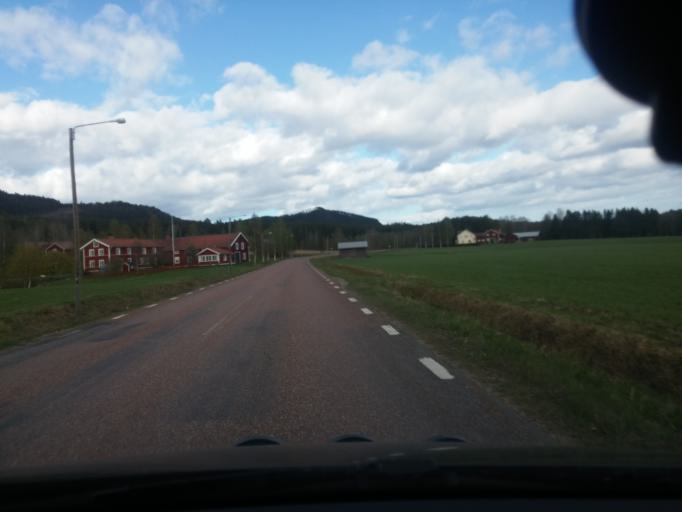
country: SE
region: Gaevleborg
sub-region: Bollnas Kommun
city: Arbra
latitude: 61.4487
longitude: 16.4689
